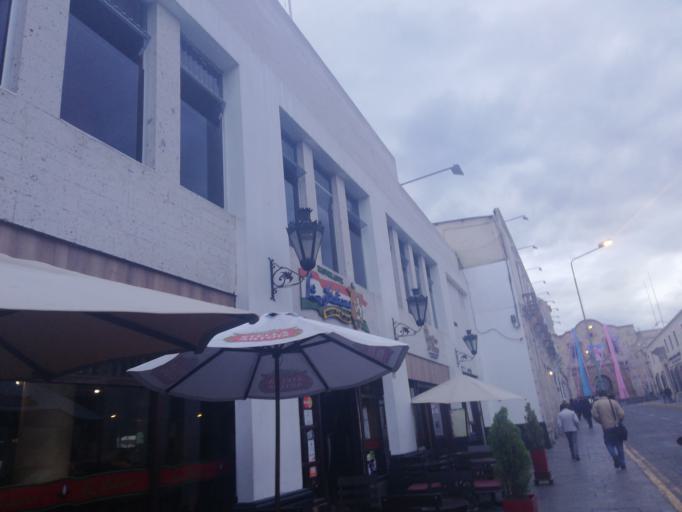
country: PE
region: Arequipa
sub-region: Provincia de Arequipa
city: Arequipa
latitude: -16.3963
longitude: -71.5354
